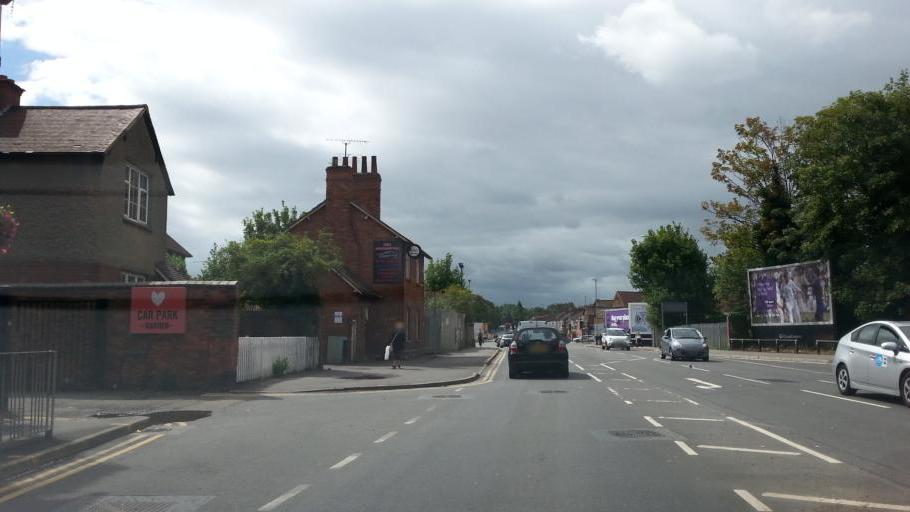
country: GB
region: England
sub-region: Northamptonshire
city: Hardingstone
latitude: 52.2294
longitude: -0.8963
